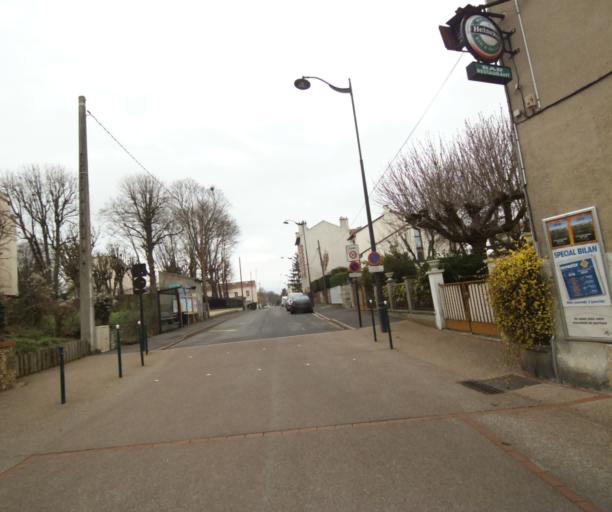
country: FR
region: Ile-de-France
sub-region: Departement des Hauts-de-Seine
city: Garches
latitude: 48.8572
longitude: 2.1901
